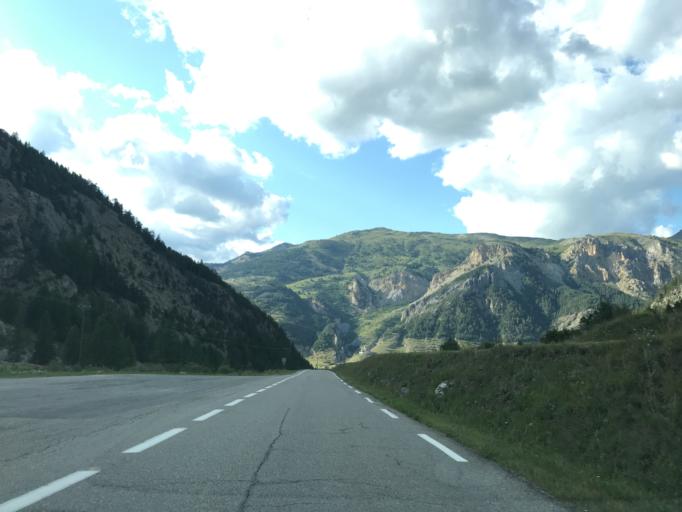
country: IT
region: Piedmont
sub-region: Provincia di Torino
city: Claviere
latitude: 44.8573
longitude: 6.7259
